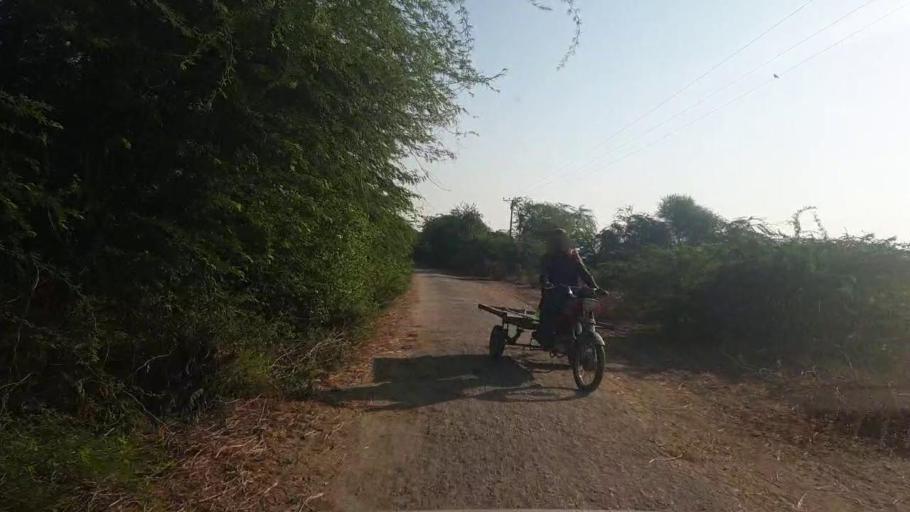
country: PK
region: Sindh
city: Badin
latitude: 24.7333
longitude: 68.8801
